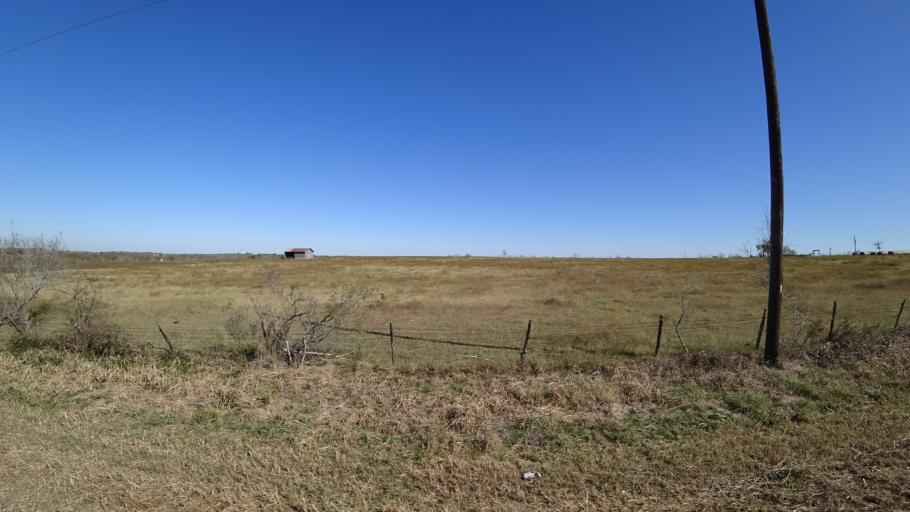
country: US
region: Texas
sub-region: Travis County
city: Garfield
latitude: 30.1053
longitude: -97.6439
